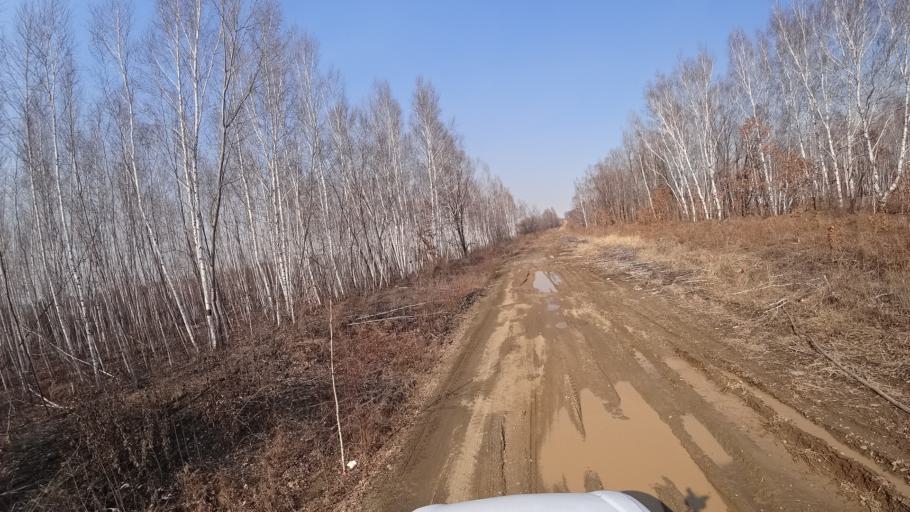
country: RU
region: Amur
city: Novobureyskiy
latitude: 49.8285
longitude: 129.9892
